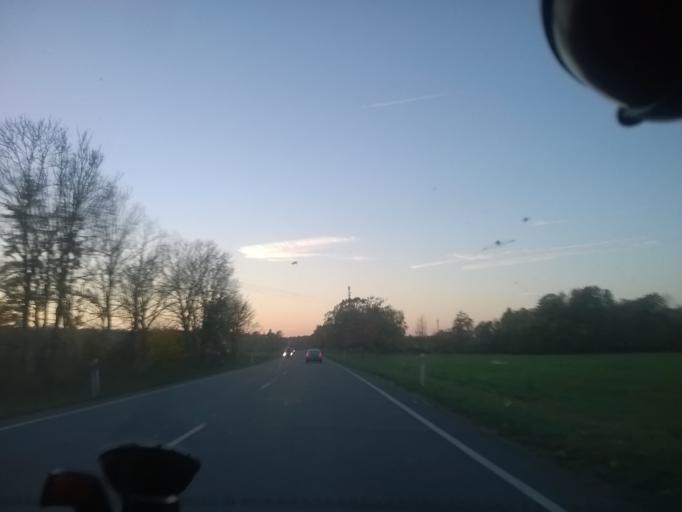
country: EE
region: Laeaene
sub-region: Ridala Parish
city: Uuemoisa
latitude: 58.9595
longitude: 23.7123
